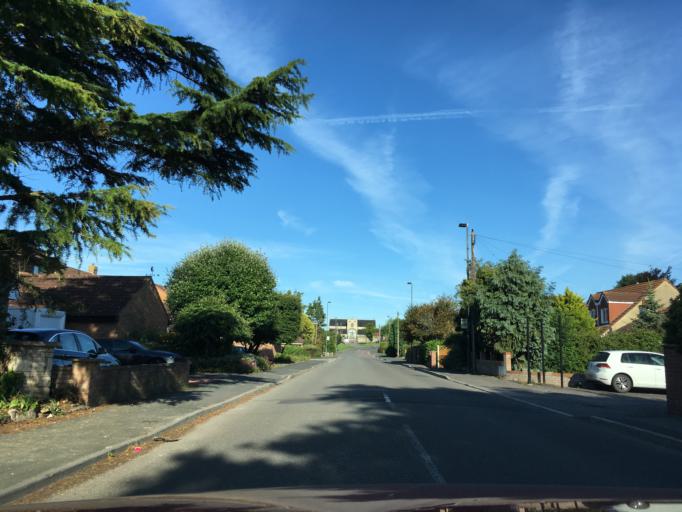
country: GB
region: England
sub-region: Bath and North East Somerset
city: Keynsham
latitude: 51.4335
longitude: -2.4969
